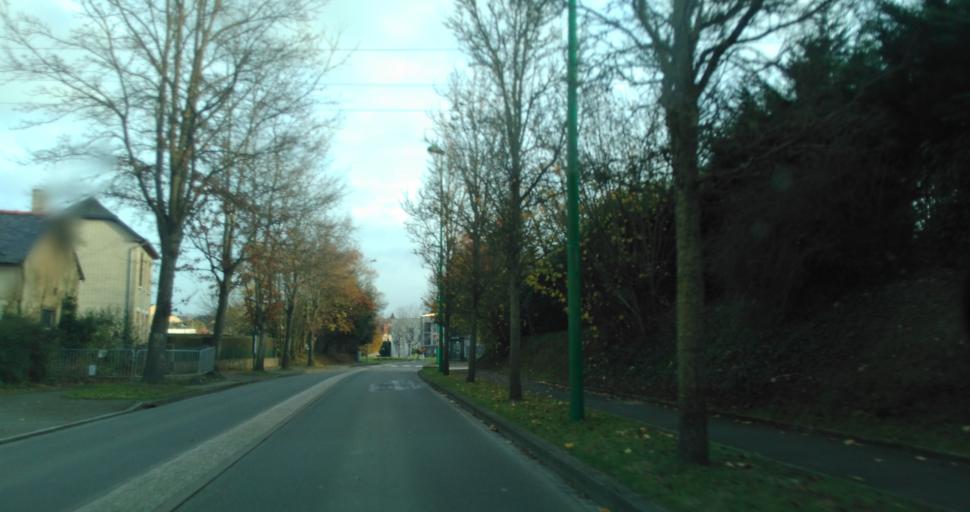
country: FR
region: Brittany
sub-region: Departement d'Ille-et-Vilaine
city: Vezin-le-Coquet
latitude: 48.1194
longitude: -1.7620
